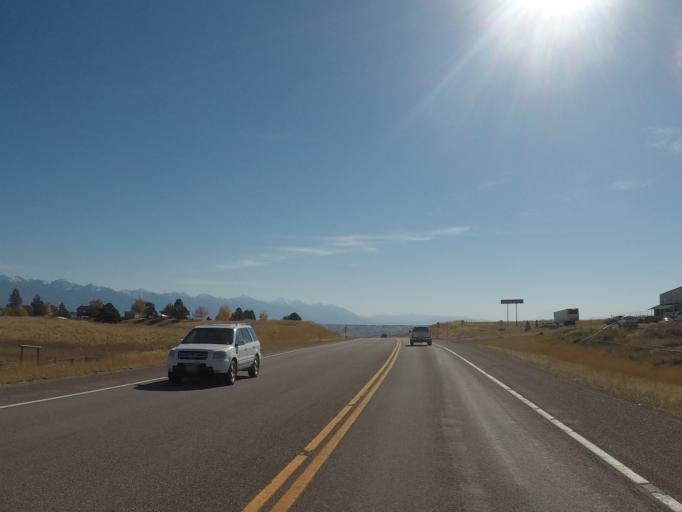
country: US
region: Montana
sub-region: Lake County
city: Polson
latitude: 47.7447
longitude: -114.2291
